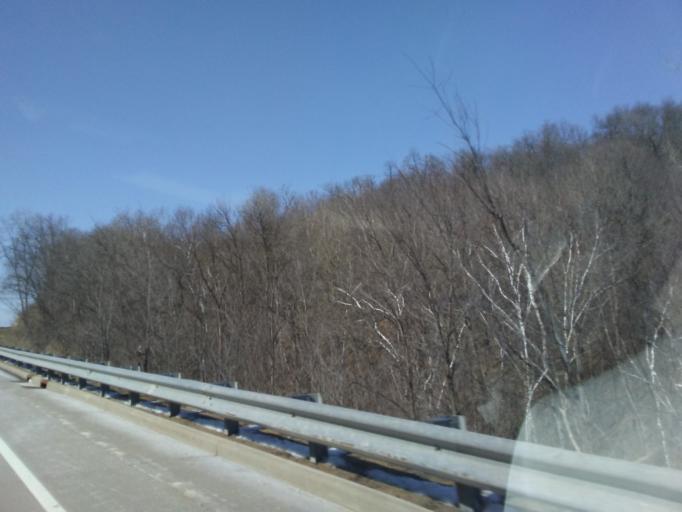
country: US
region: Wisconsin
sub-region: La Crosse County
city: West Salem
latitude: 43.7096
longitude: -91.0603
